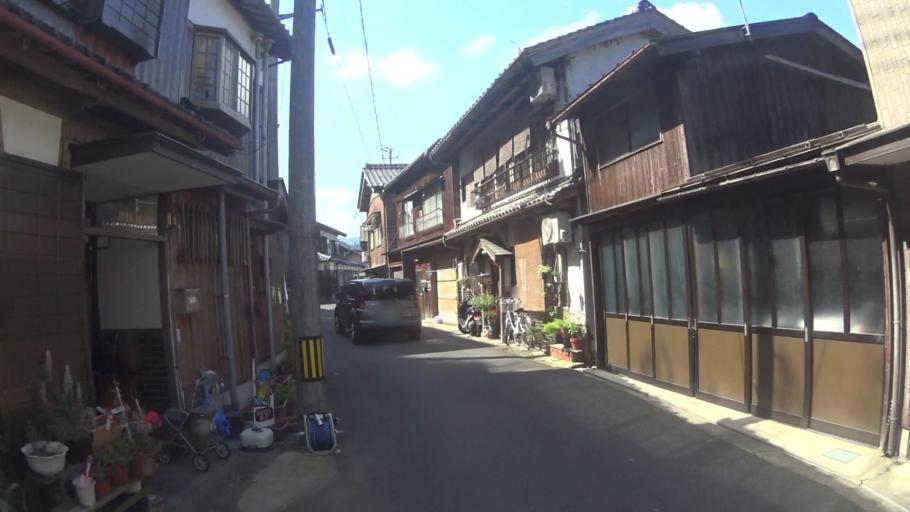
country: JP
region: Kyoto
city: Miyazu
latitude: 35.6661
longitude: 135.2901
